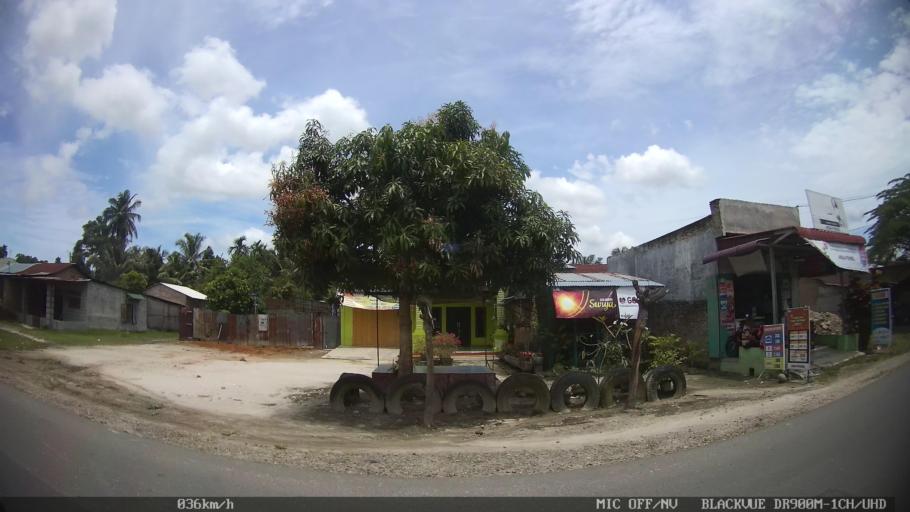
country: ID
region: North Sumatra
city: Percut
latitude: 3.5817
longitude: 98.8832
